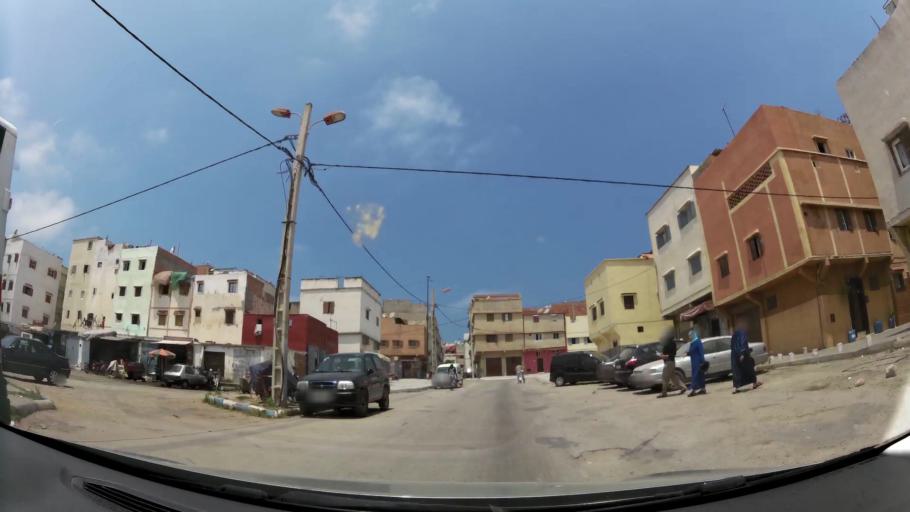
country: MA
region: Rabat-Sale-Zemmour-Zaer
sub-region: Rabat
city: Rabat
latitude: 33.9846
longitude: -6.8807
